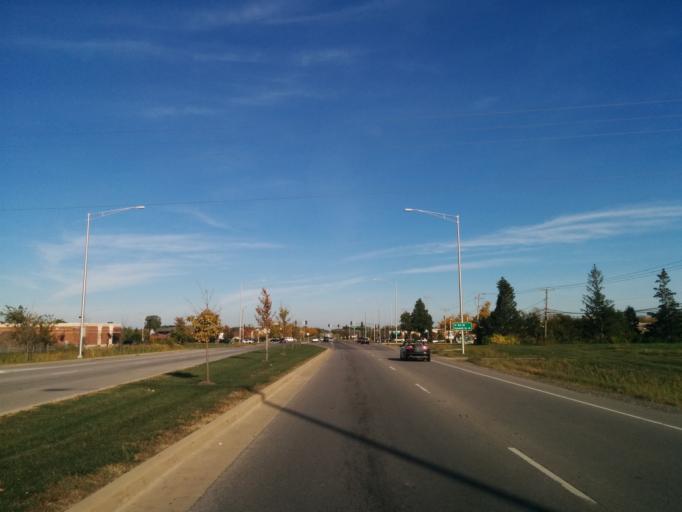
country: US
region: Illinois
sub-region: Kane County
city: North Aurora
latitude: 41.8128
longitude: -88.2826
